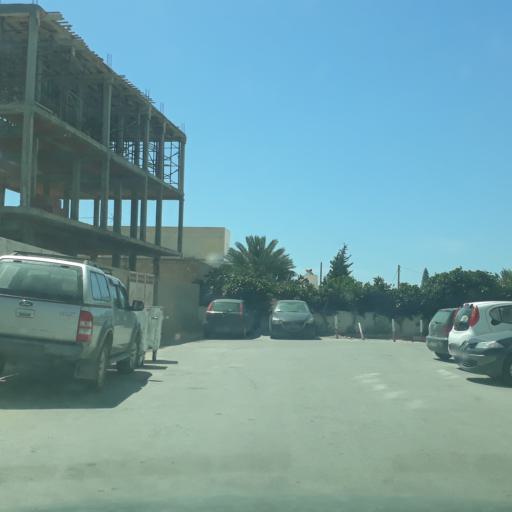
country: TN
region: Safaqis
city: Al Qarmadah
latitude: 34.7990
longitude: 10.7579
